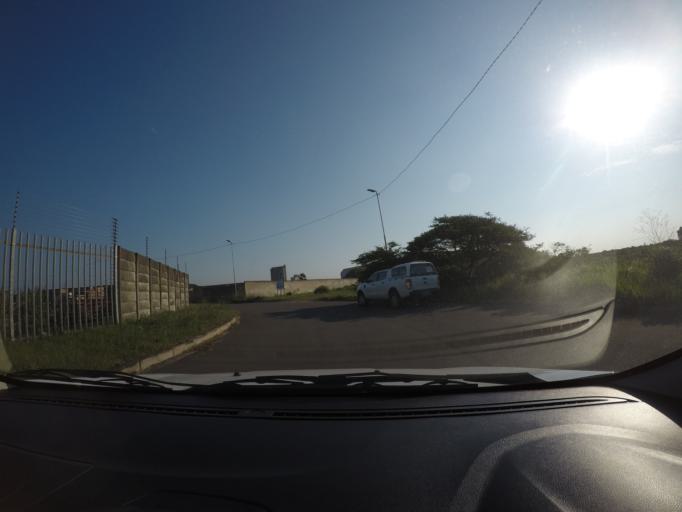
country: ZA
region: KwaZulu-Natal
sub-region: uThungulu District Municipality
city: Richards Bay
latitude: -28.7510
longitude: 32.0152
